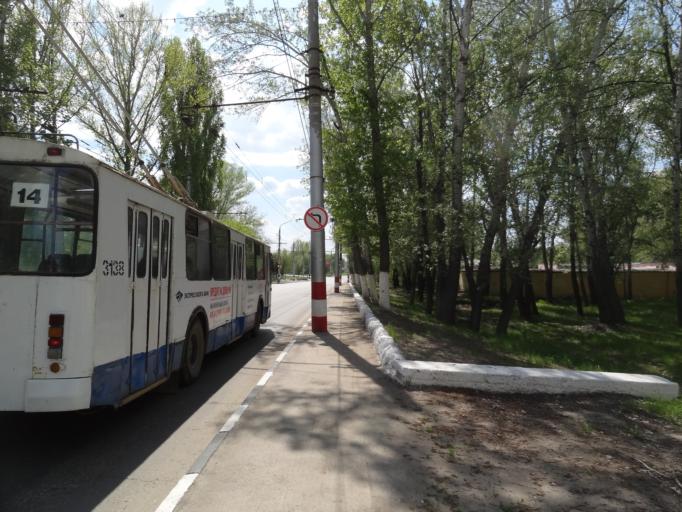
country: RU
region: Saratov
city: Engel's
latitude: 51.5017
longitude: 46.1034
